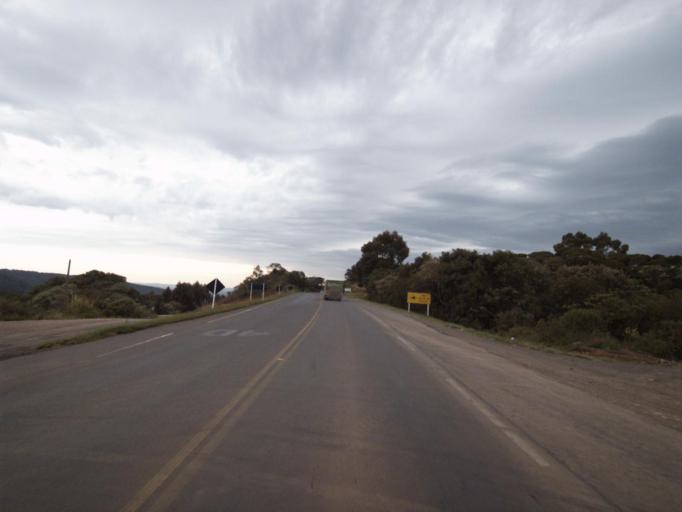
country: BR
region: Santa Catarina
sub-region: Concordia
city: Concordia
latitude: -27.0284
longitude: -51.8830
